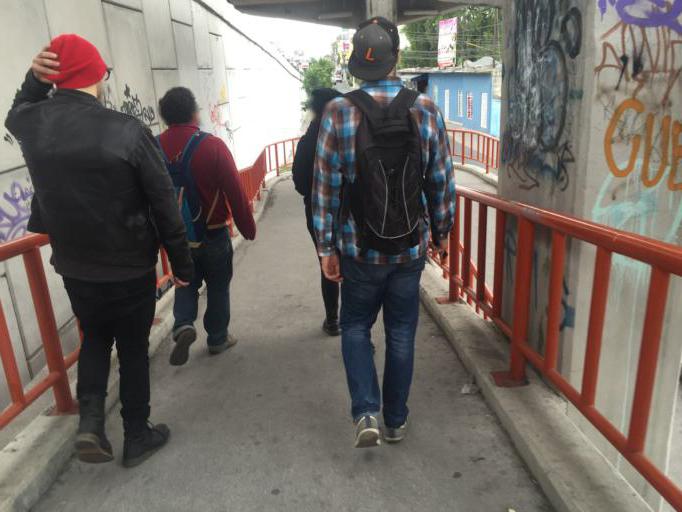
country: MX
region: Mexico
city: Ecatepec
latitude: 19.6007
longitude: -99.0395
